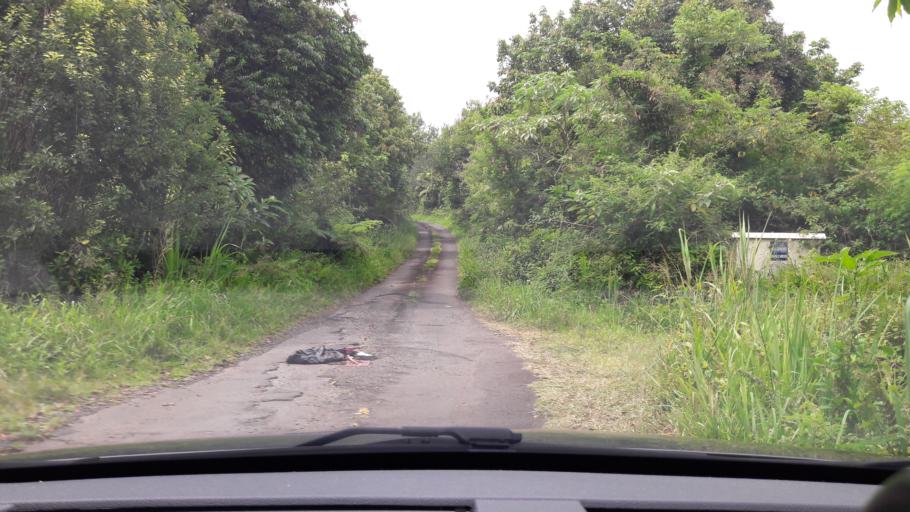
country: RE
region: Reunion
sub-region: Reunion
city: Saint-Benoit
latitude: -21.0991
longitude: 55.6965
